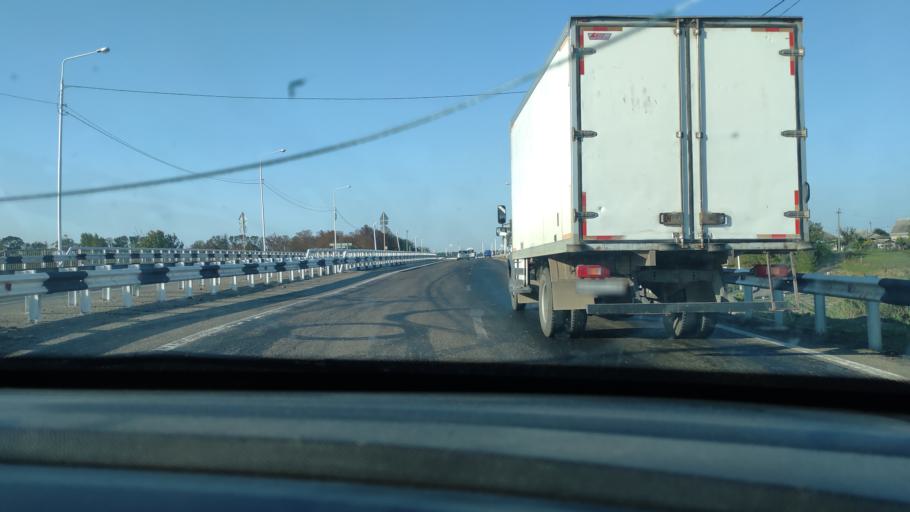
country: RU
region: Krasnodarskiy
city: Timashevsk
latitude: 45.5180
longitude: 38.9409
